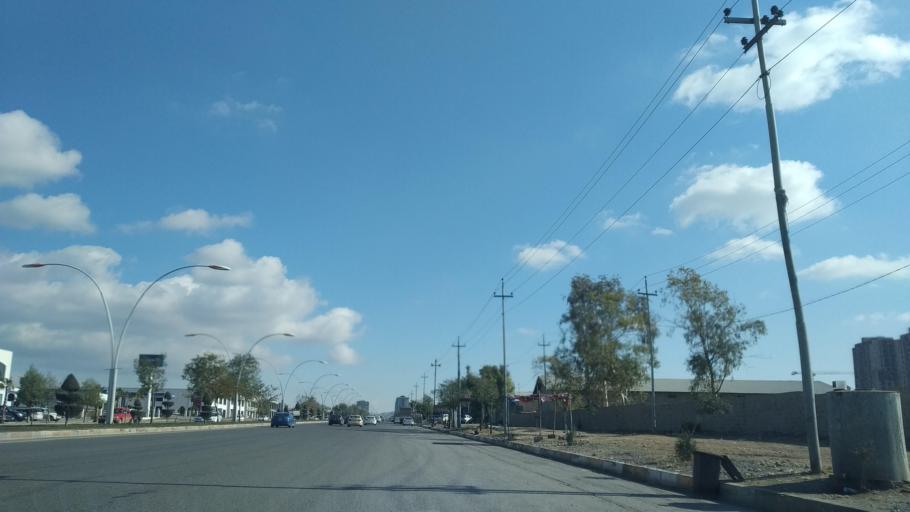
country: IQ
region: Arbil
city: Erbil
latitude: 36.2014
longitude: 44.0991
